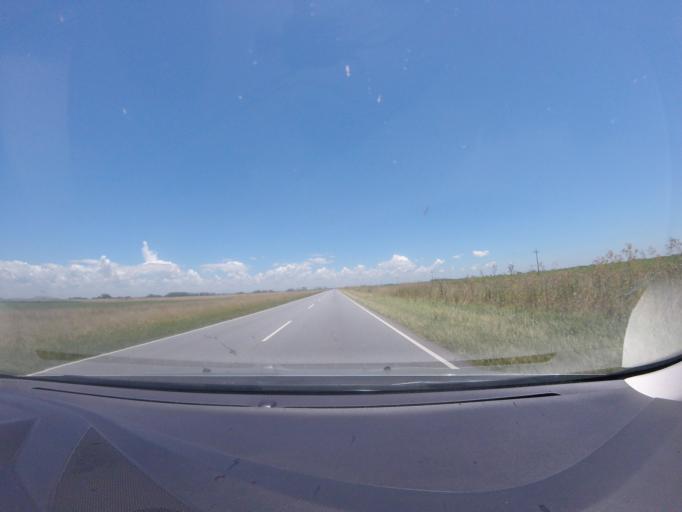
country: AR
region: Buenos Aires
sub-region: Partido de Tandil
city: Tandil
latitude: -37.1510
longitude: -59.0070
